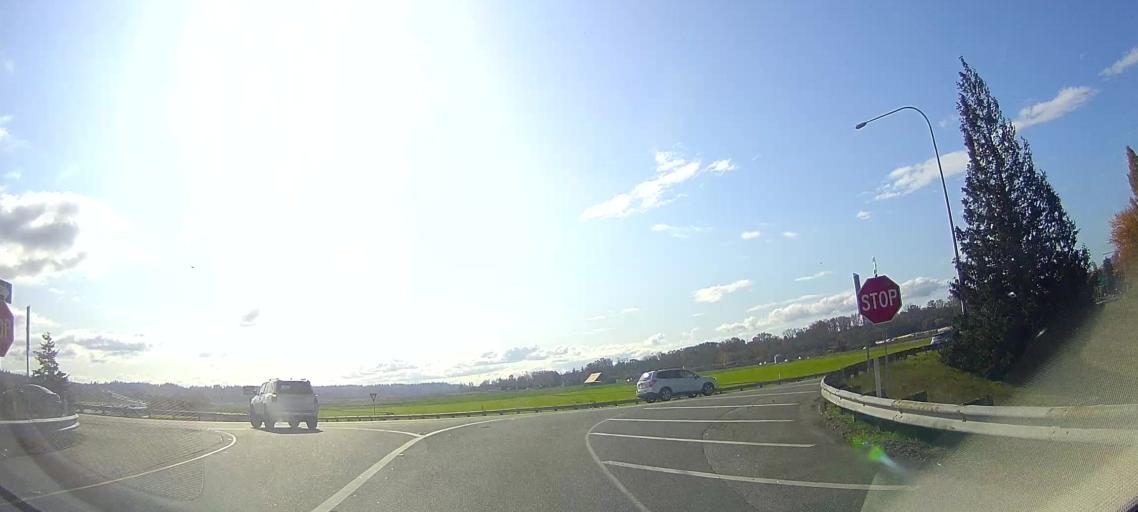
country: US
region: Washington
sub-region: Skagit County
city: Mount Vernon
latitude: 48.3416
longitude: -122.3368
